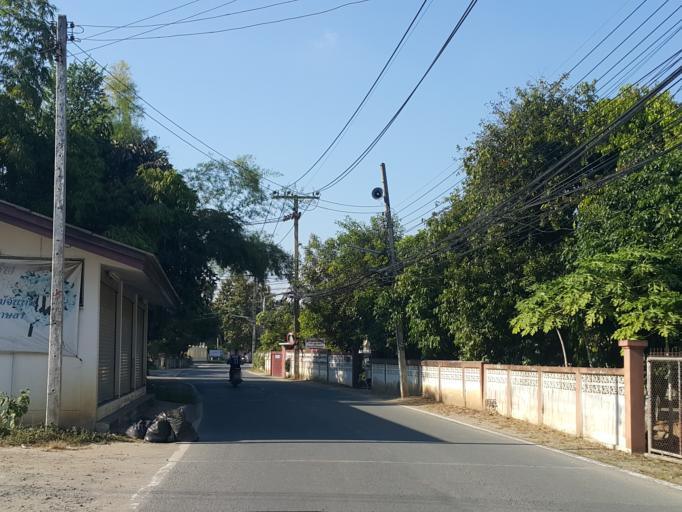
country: TH
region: Chiang Mai
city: San Sai
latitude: 18.7895
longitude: 99.0475
